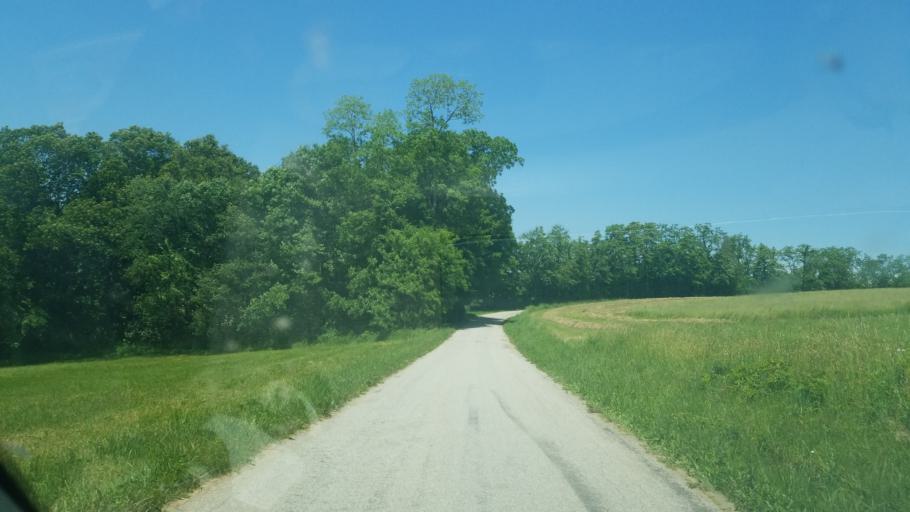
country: US
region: Ohio
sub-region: Sandusky County
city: Bellville
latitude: 40.6202
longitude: -82.4655
